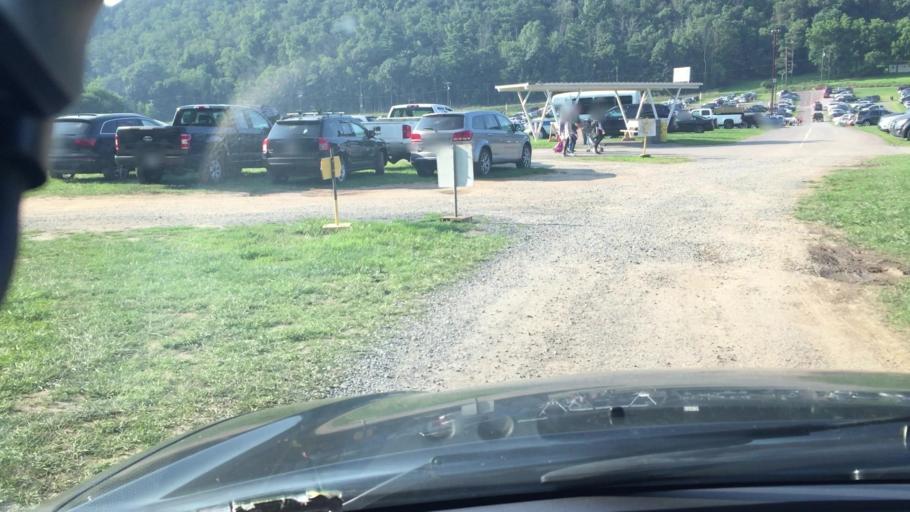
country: US
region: Pennsylvania
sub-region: Northumberland County
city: Elysburg
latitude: 40.8771
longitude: -76.4977
